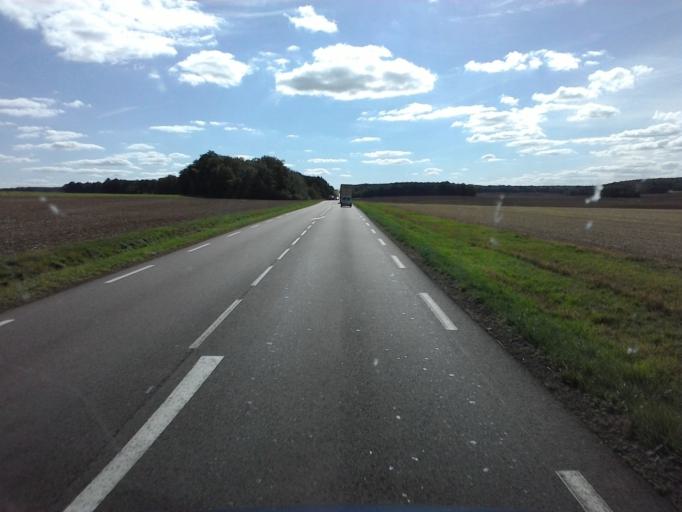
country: FR
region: Bourgogne
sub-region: Departement de la Cote-d'Or
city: Chatillon-sur-Seine
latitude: 47.8016
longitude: 4.5233
